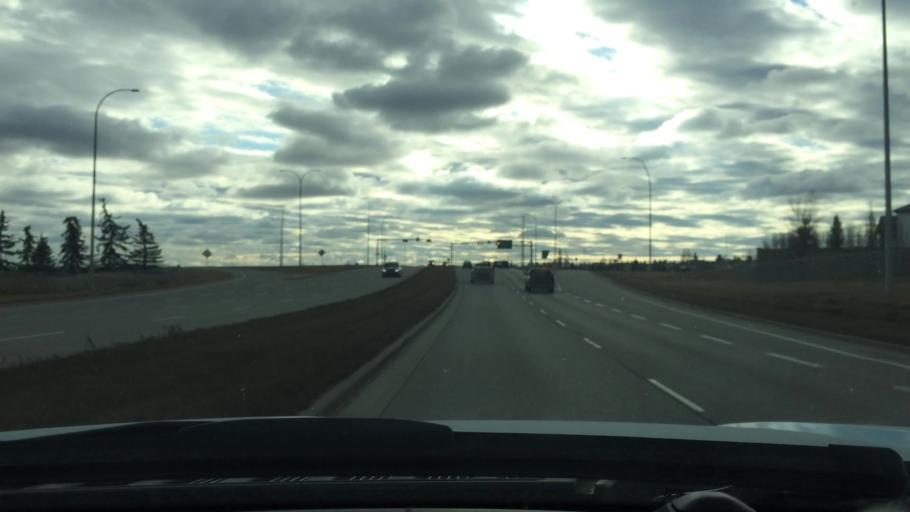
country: CA
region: Alberta
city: Calgary
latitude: 51.1464
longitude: -114.0954
